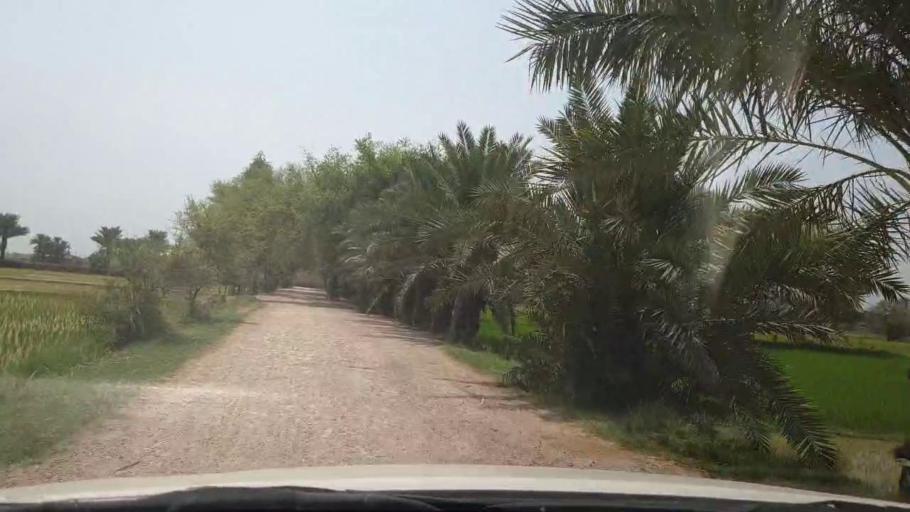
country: PK
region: Sindh
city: Rustam jo Goth
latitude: 28.0058
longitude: 68.7687
